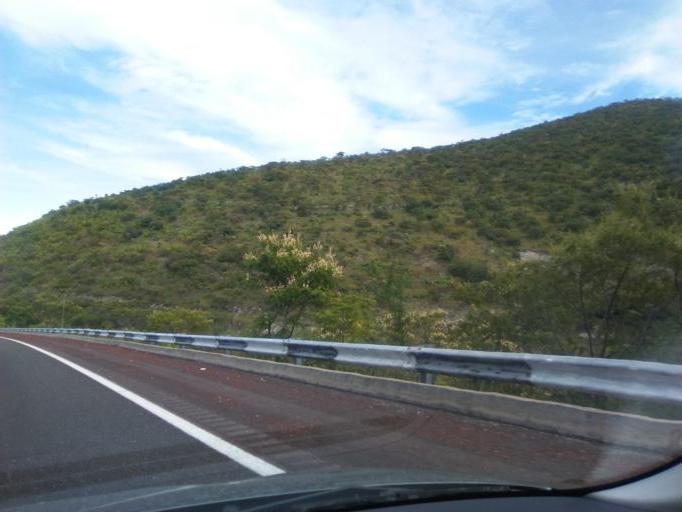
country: MX
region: Guerrero
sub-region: Eduardo Neri
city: Tlanipatla
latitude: 17.8531
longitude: -99.4285
